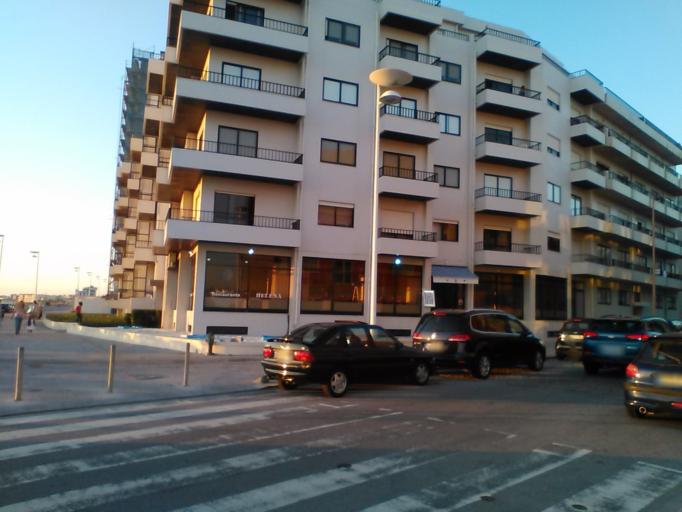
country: PT
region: Porto
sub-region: Vila do Conde
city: Vila do Conde
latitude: 41.3511
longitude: -8.7537
